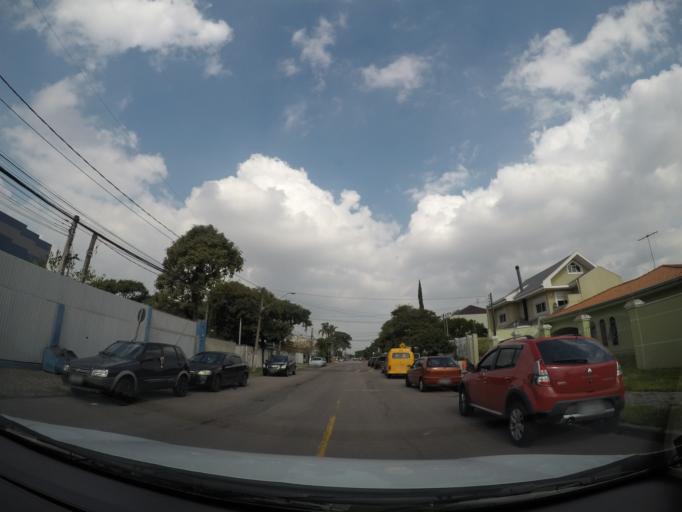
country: BR
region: Parana
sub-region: Curitiba
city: Curitiba
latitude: -25.4766
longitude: -49.2551
